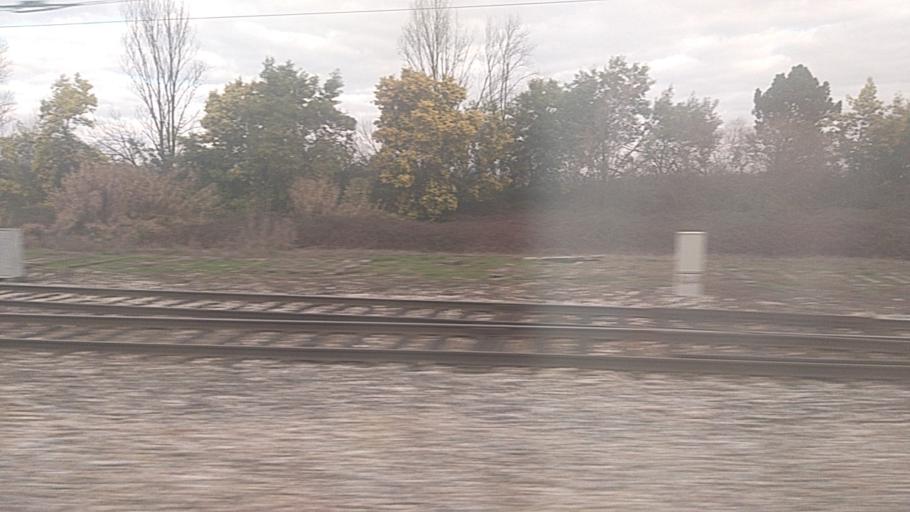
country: PT
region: Coimbra
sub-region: Soure
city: Alfarelos
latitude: 40.1662
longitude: -8.6323
